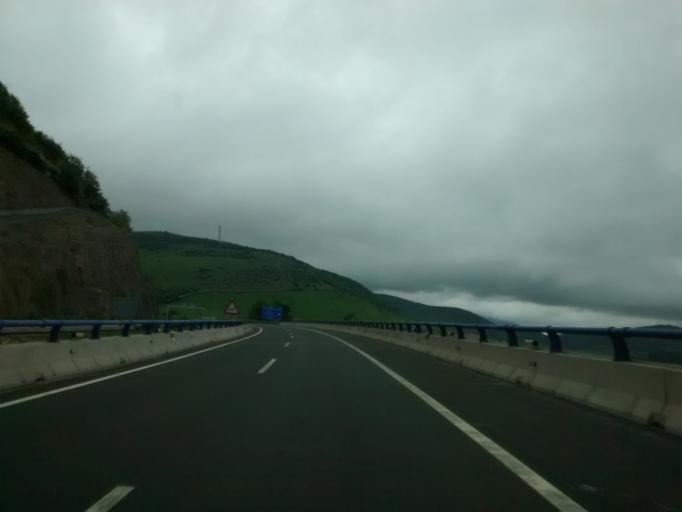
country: ES
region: Cantabria
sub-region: Provincia de Cantabria
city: Santiurde de Reinosa
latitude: 43.0545
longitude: -4.0867
